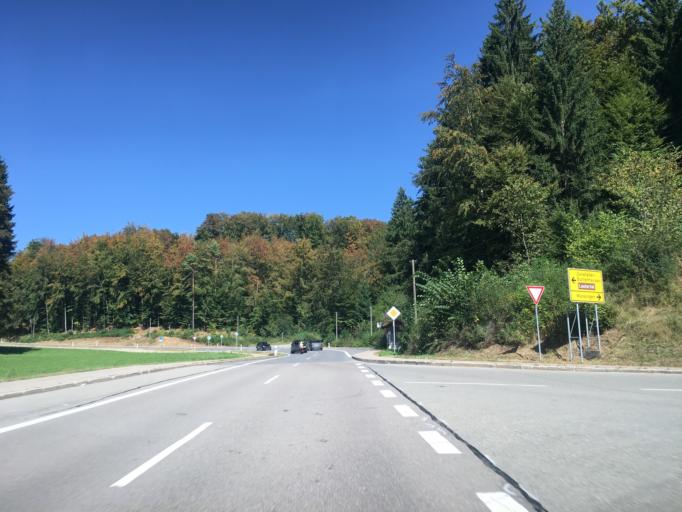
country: DE
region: Baden-Wuerttemberg
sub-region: Tuebingen Region
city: Munsingen
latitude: 48.3820
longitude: 9.4863
